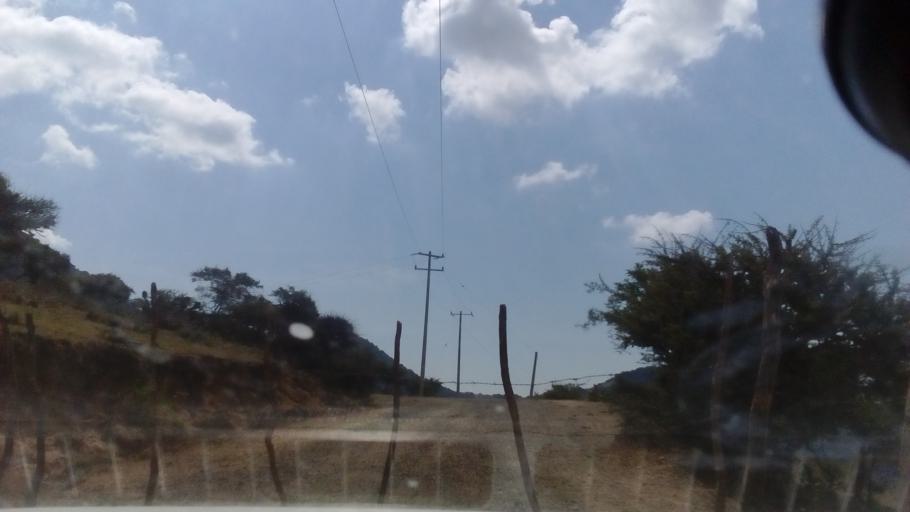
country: MX
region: Guanajuato
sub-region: Silao de la Victoria
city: San Francisco (Banos de Agua Caliente)
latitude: 21.1597
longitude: -101.4603
